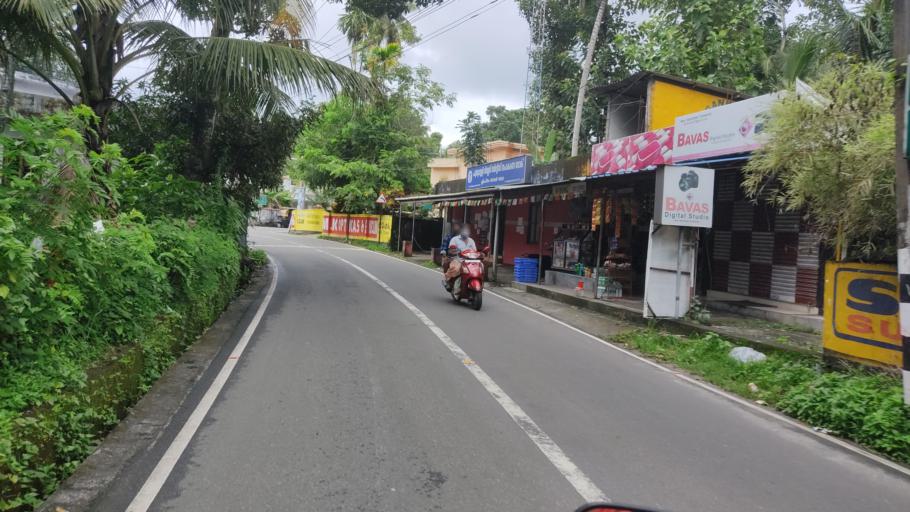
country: IN
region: Kerala
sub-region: Alappuzha
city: Kayankulam
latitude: 9.1641
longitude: 76.4913
